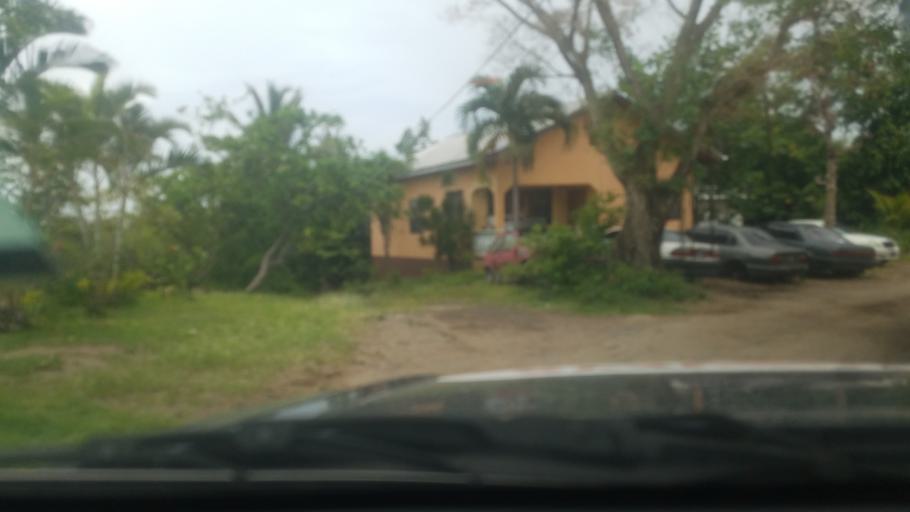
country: LC
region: Laborie Quarter
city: Laborie
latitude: 13.7493
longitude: -60.9788
